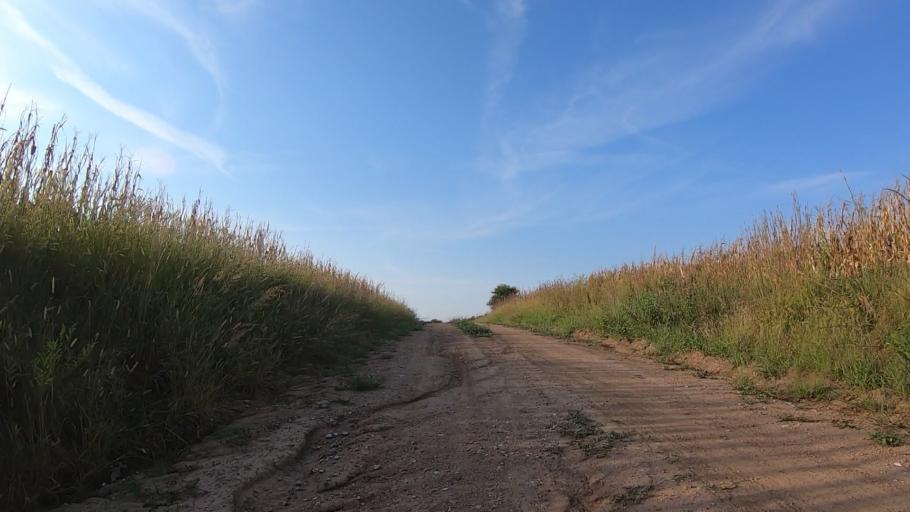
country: US
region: Kansas
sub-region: Marshall County
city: Blue Rapids
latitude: 39.7031
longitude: -96.7792
